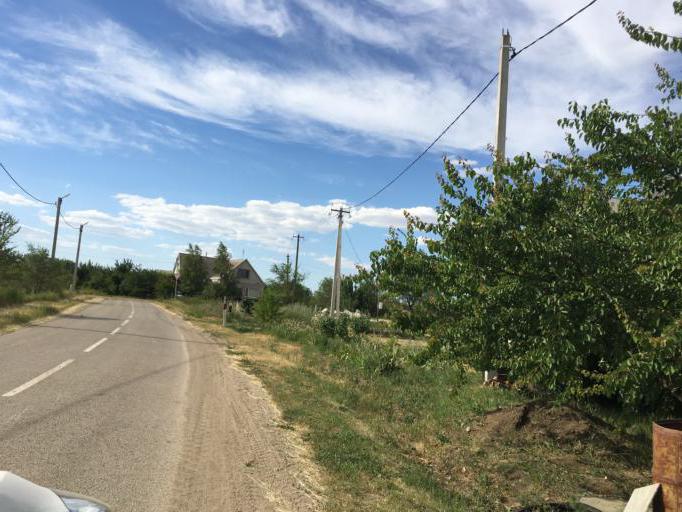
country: RU
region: Krasnodarskiy
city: Kushchevskaya
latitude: 46.5550
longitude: 39.6737
